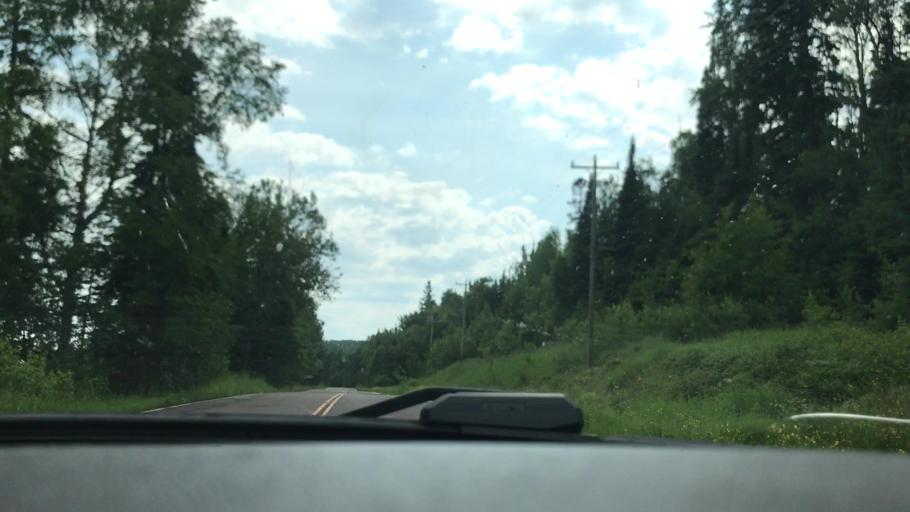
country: CA
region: Ontario
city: Neebing
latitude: 47.9575
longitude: -89.6911
